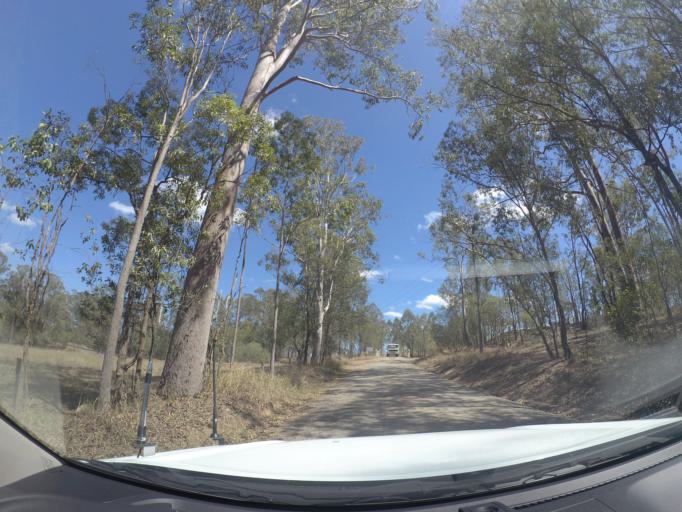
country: AU
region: Queensland
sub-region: Logan
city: North Maclean
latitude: -27.8379
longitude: 152.9268
